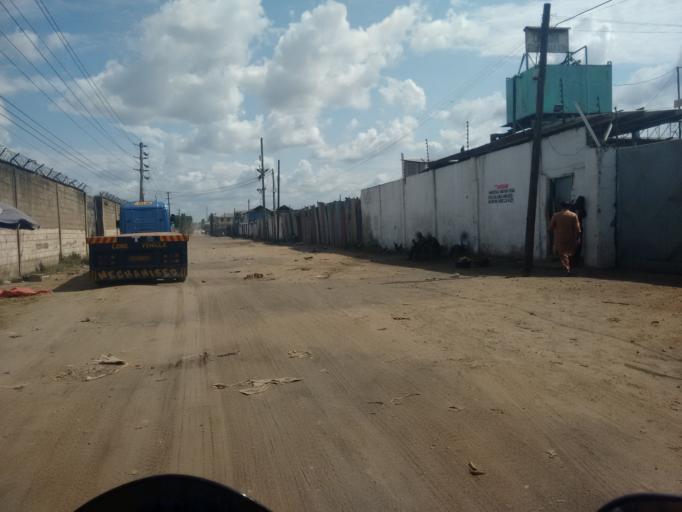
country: TZ
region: Dar es Salaam
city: Dar es Salaam
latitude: -6.8427
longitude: 39.2643
